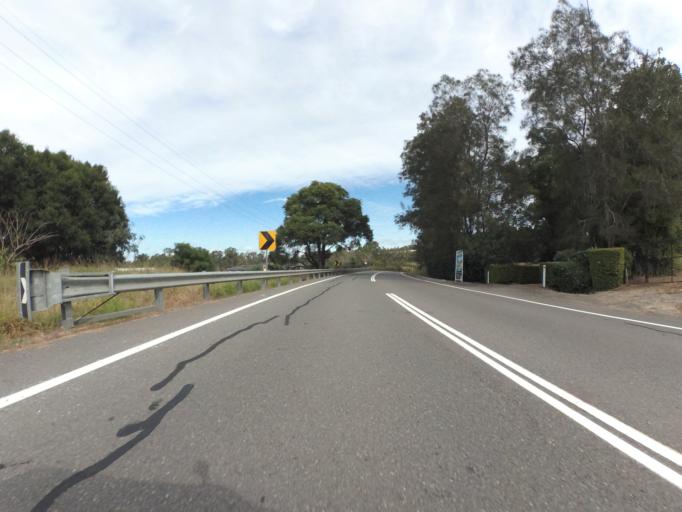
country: AU
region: Queensland
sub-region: Ipswich
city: Redbank
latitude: -27.5938
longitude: 152.8598
